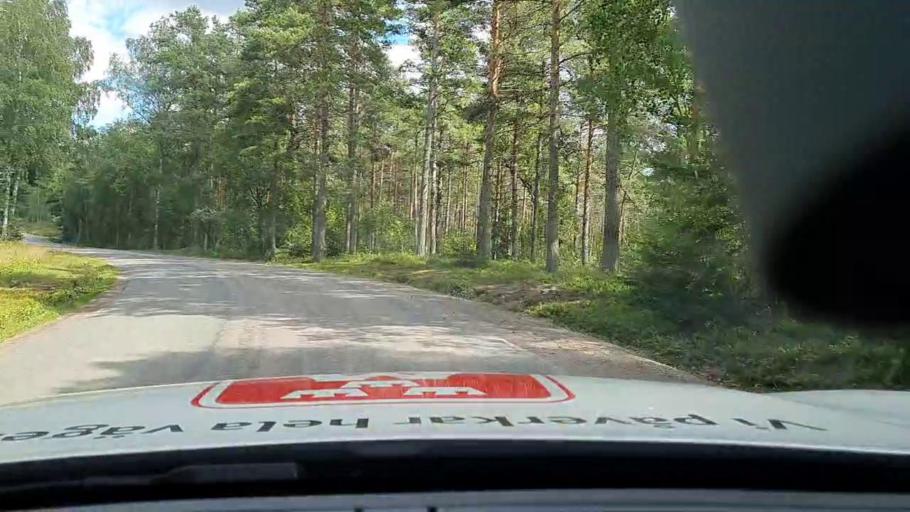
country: SE
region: Vaestra Goetaland
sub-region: Karlsborgs Kommun
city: Molltorp
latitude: 58.6026
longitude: 14.3747
